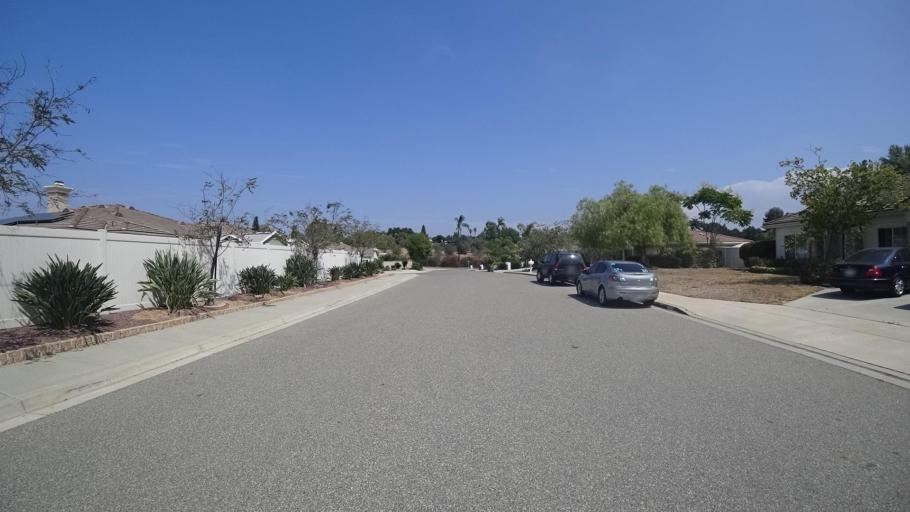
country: US
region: California
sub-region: San Diego County
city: Fallbrook
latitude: 33.3532
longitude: -117.2379
